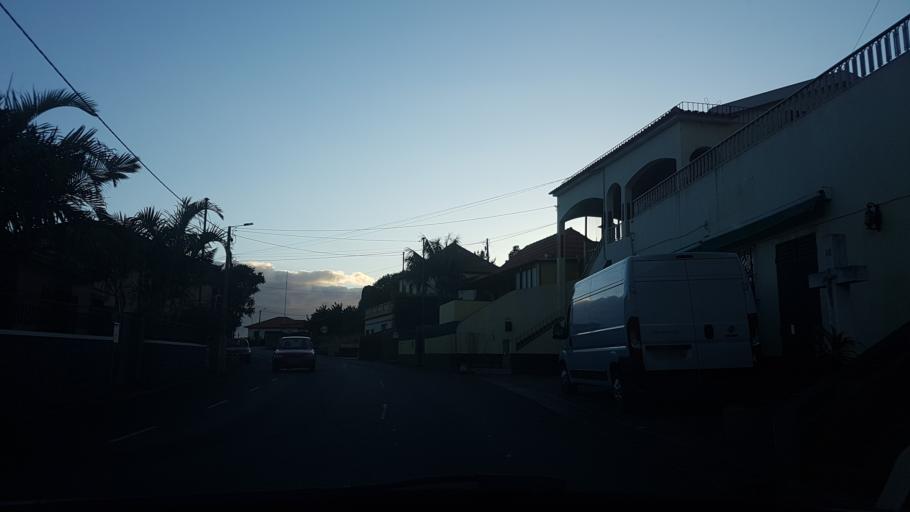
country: PT
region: Madeira
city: Ponta do Sol
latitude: 32.6984
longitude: -17.1153
